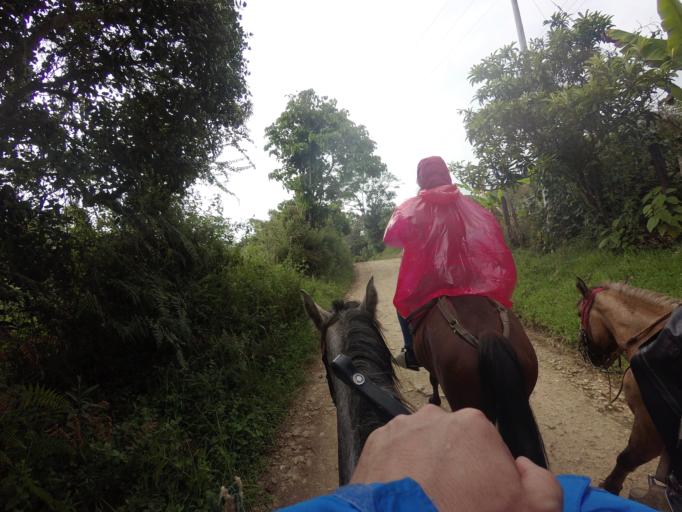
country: CO
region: Huila
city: San Agustin
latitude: 1.9040
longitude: -76.2939
